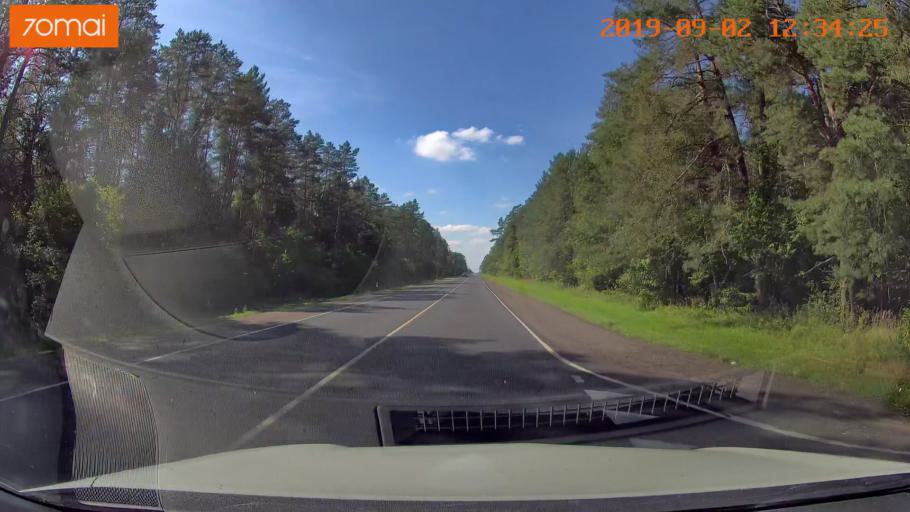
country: RU
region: Smolensk
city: Shumyachi
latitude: 53.8105
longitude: 32.4050
